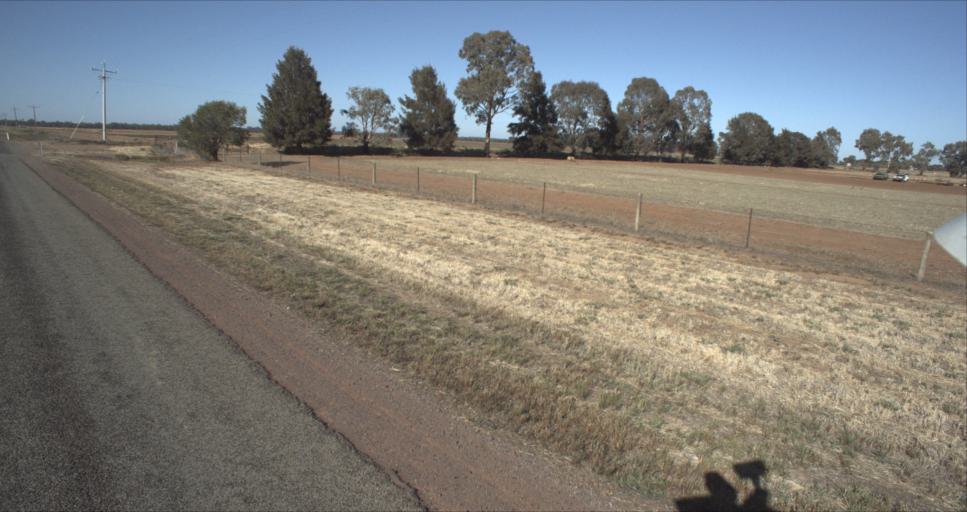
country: AU
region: New South Wales
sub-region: Leeton
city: Leeton
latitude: -34.5875
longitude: 146.2603
